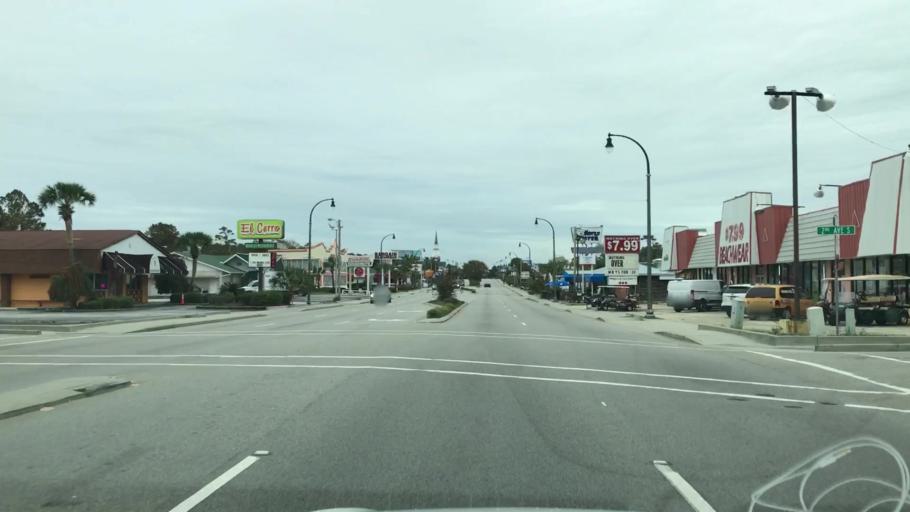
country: US
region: South Carolina
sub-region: Horry County
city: Myrtle Beach
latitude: 33.6851
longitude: -78.8911
